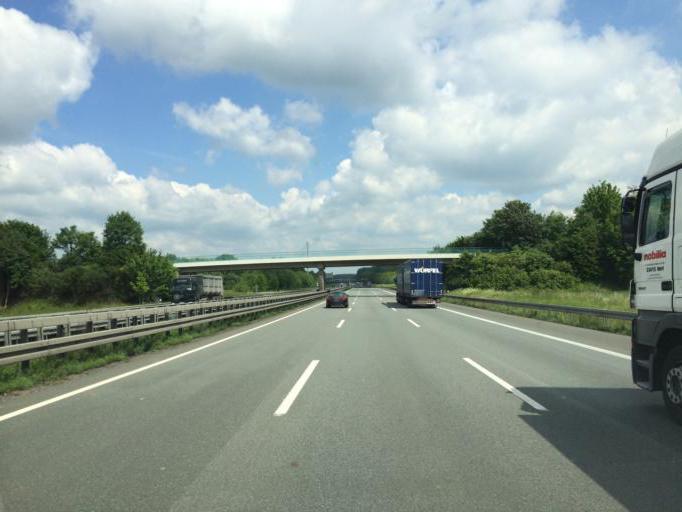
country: DE
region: North Rhine-Westphalia
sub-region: Regierungsbezirk Arnsberg
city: Hamm
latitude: 51.6350
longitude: 7.8850
